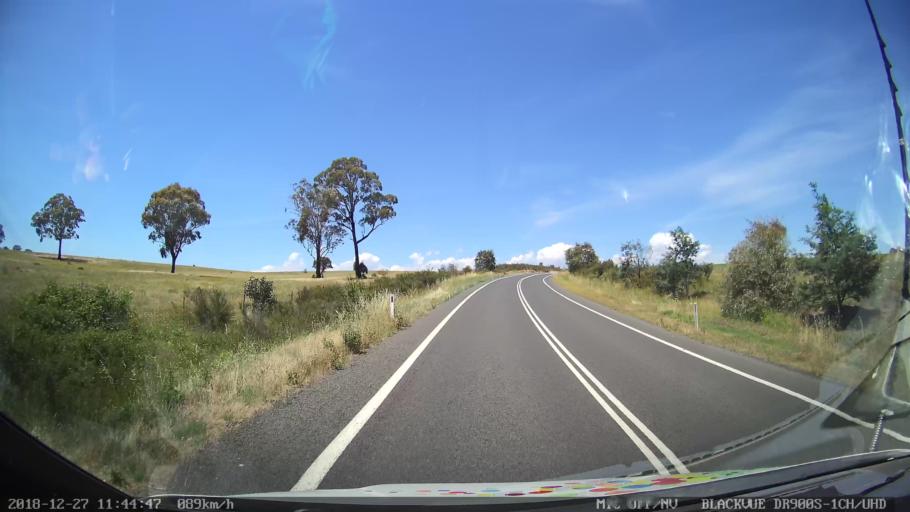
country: AU
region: New South Wales
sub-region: Bathurst Regional
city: Perthville
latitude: -33.5763
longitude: 149.4763
